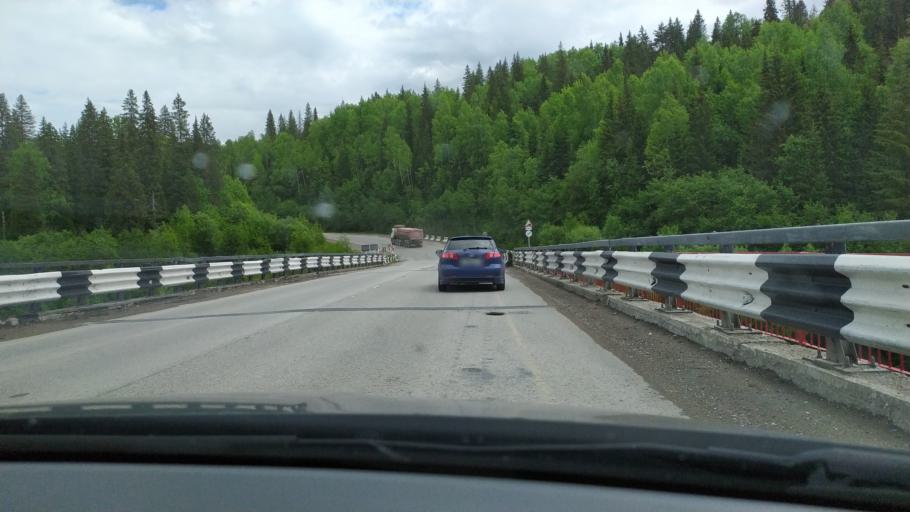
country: RU
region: Perm
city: Gremyachinsk
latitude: 58.4416
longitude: 57.8762
